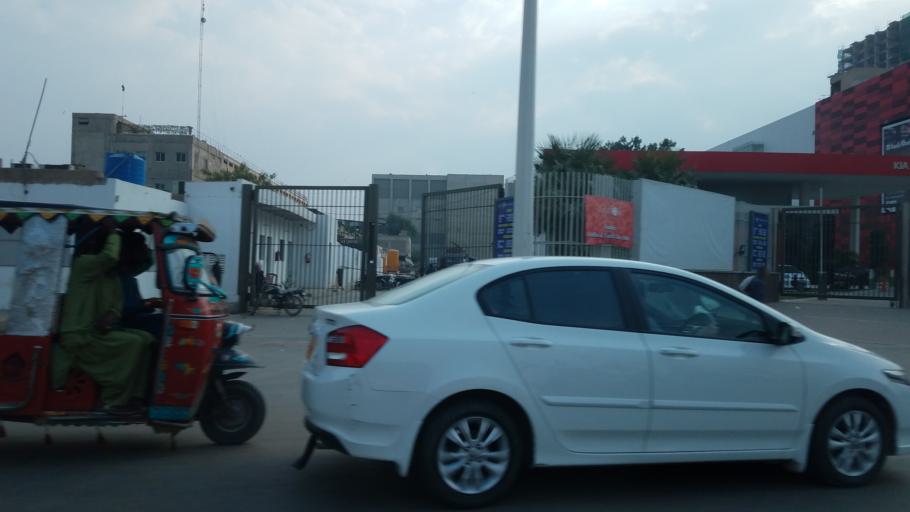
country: PK
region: Sindh
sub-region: Karachi District
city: Karachi
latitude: 24.9334
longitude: 67.0857
